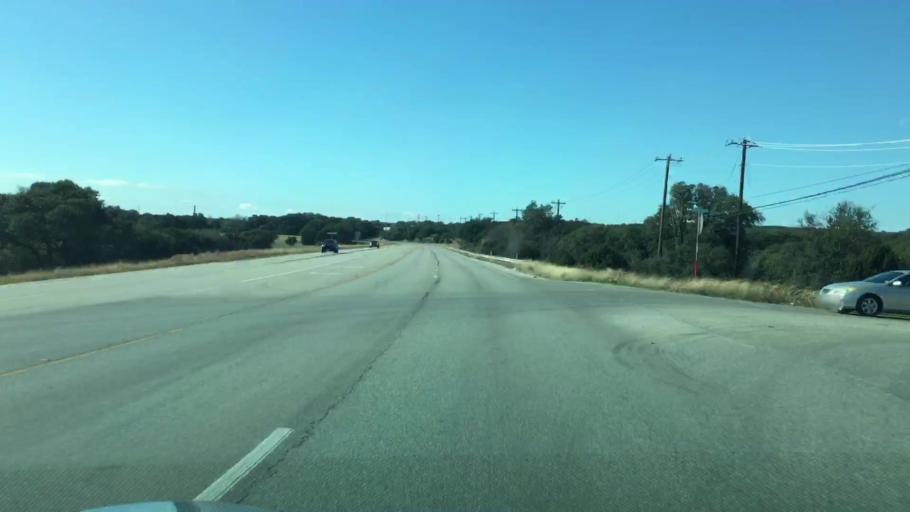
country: US
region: Texas
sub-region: Hays County
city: Dripping Springs
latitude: 30.2067
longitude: -98.1426
